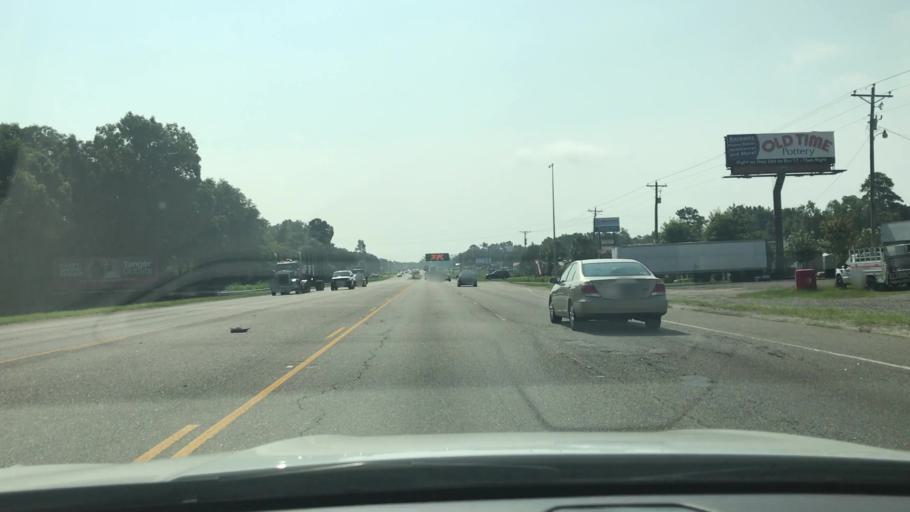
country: US
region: South Carolina
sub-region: Horry County
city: Red Hill
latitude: 33.8130
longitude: -79.0334
